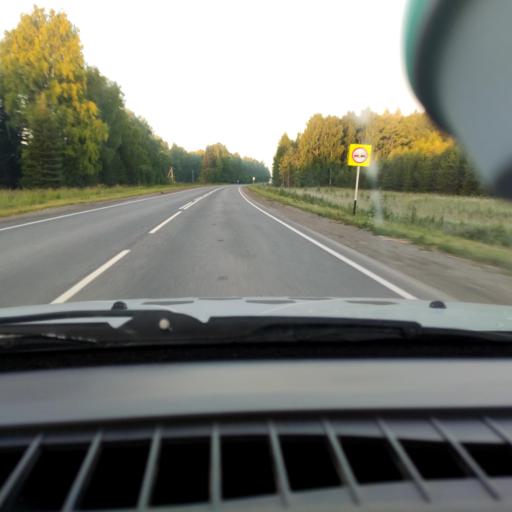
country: RU
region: Perm
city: Orda
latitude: 57.2498
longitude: 56.9981
